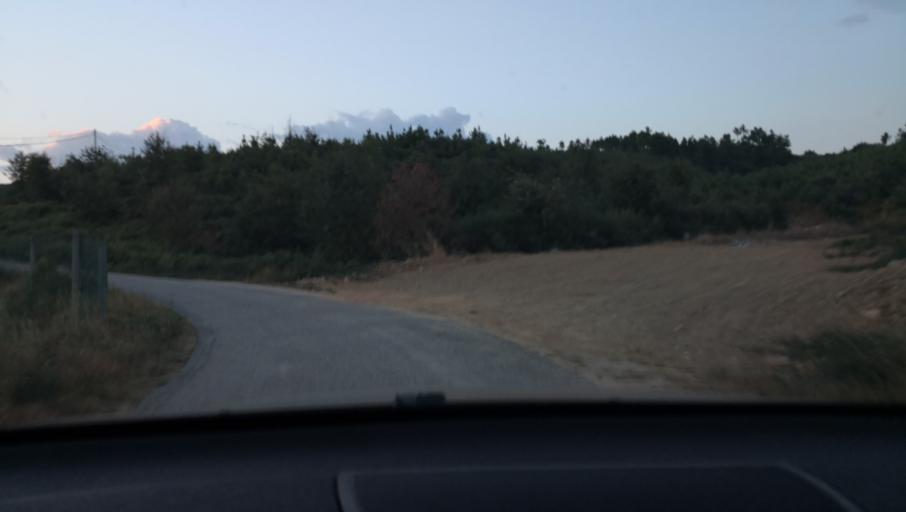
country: PT
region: Vila Real
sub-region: Sabrosa
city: Sabrosa
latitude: 41.2714
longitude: -7.6235
